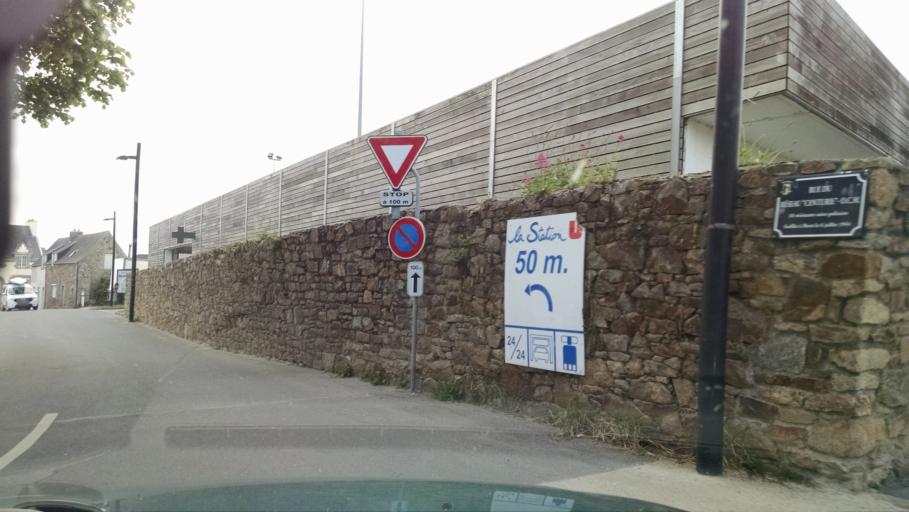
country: FR
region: Brittany
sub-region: Departement du Finistere
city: Saint-Pol-de-Leon
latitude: 48.6872
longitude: -3.9869
